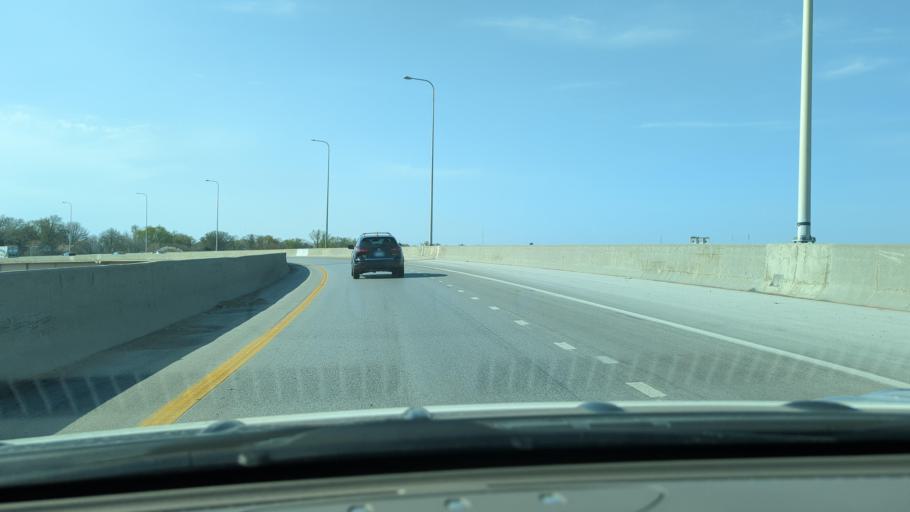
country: US
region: Nebraska
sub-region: Douglas County
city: Omaha
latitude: 41.2275
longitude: -95.9531
